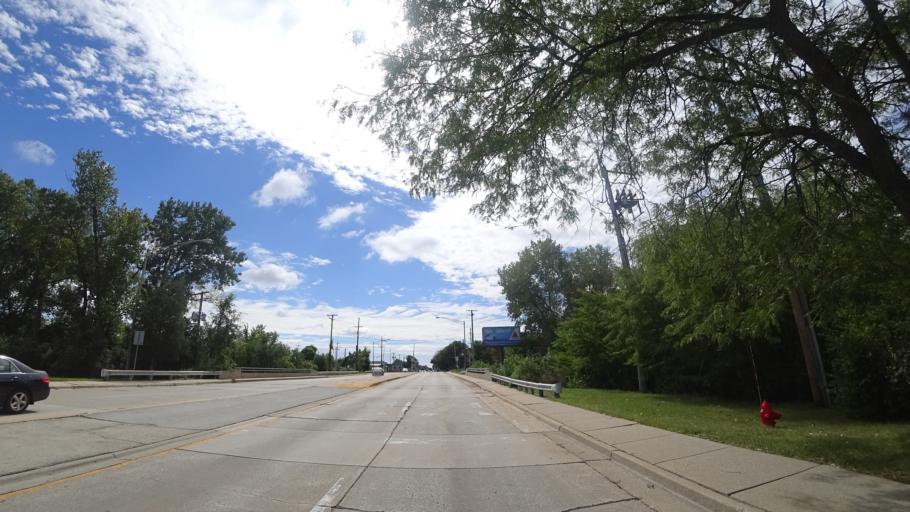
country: US
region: Illinois
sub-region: Cook County
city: Chicago Ridge
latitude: 41.7080
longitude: -87.7796
